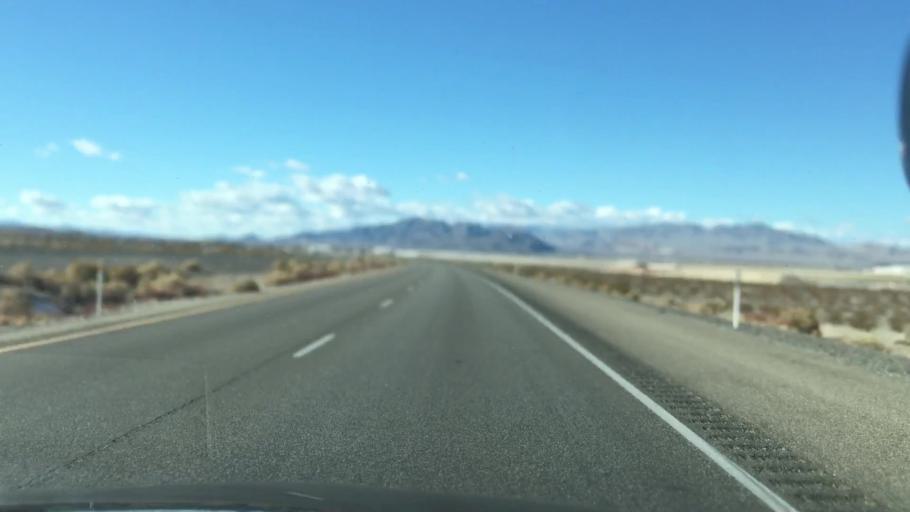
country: US
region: Nevada
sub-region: Nye County
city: Pahrump
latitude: 36.5760
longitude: -115.6418
